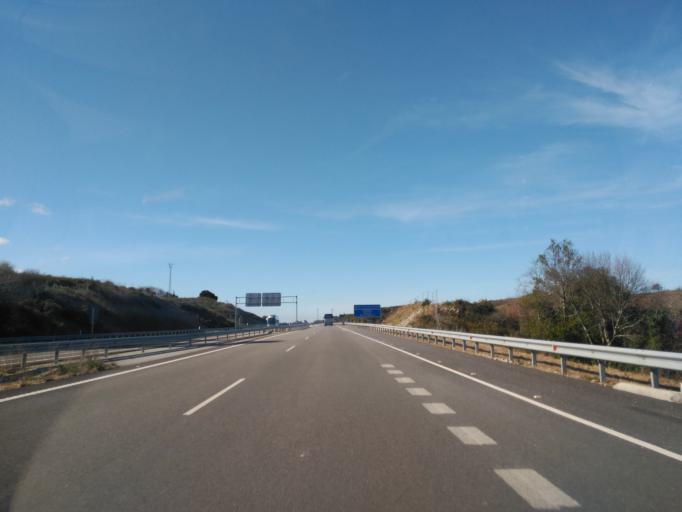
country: ES
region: Asturias
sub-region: Province of Asturias
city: Llanes
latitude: 43.3978
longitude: -4.6576
